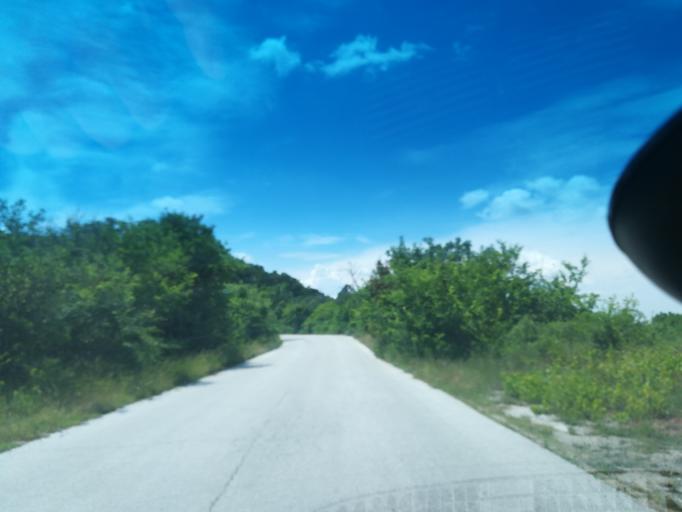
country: BG
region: Khaskovo
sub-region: Obshtina Mineralni Bani
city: Mineralni Bani
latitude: 41.9833
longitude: 25.2457
